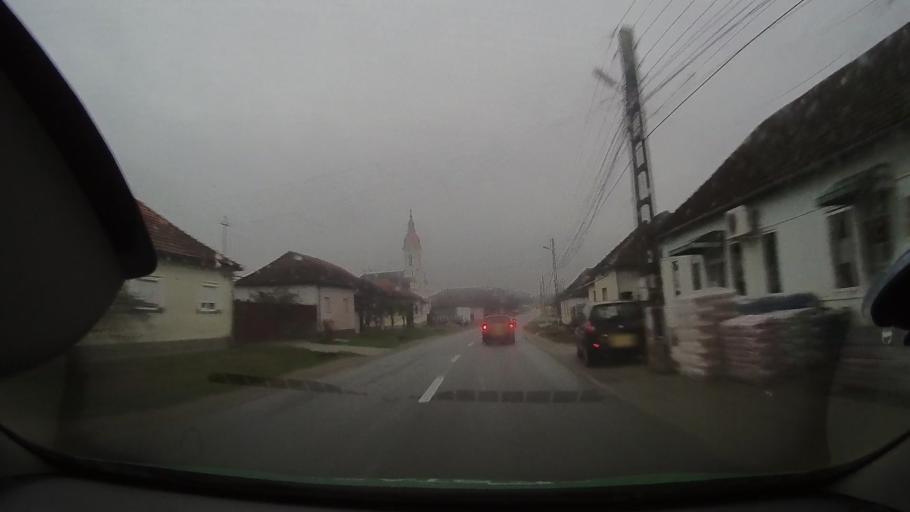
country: RO
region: Arad
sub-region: Comuna Craiova
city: Craiova
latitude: 46.5836
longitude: 21.9734
